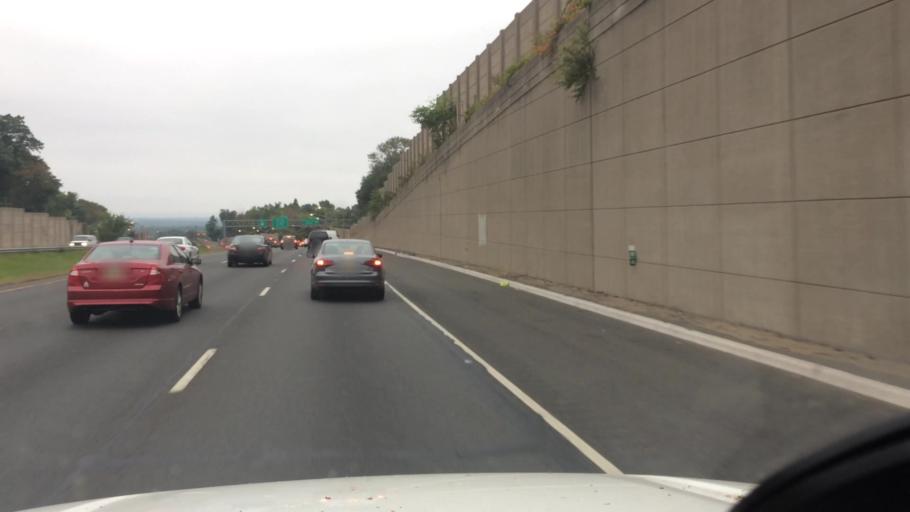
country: US
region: New Jersey
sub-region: Union County
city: Summit
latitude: 40.7296
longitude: -74.3476
